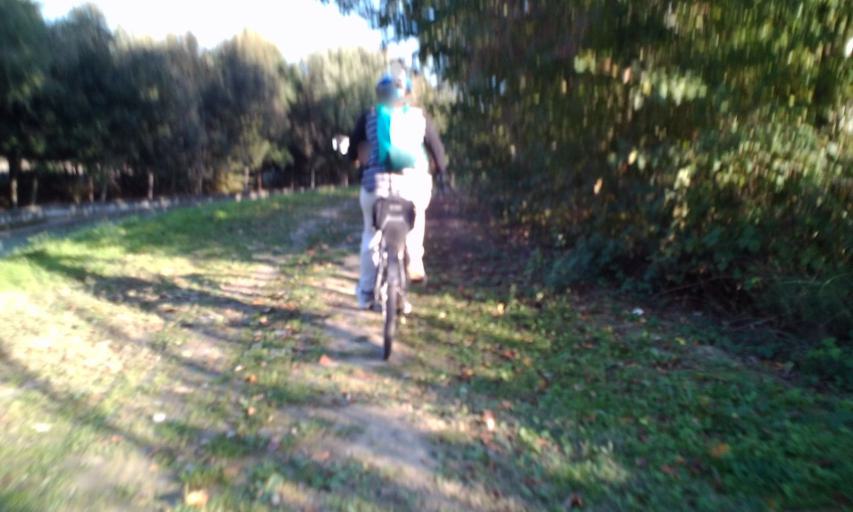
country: IT
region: Lombardy
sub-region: Provincia di Mantova
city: Serravalle a Po
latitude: 45.0979
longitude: 11.0968
